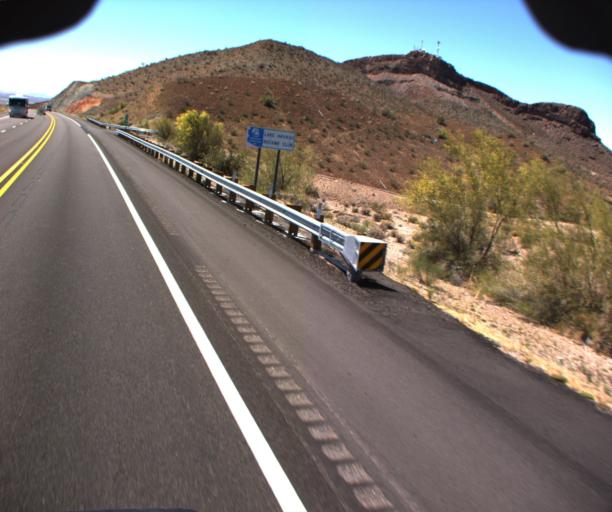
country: US
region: Arizona
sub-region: Mohave County
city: Desert Hills
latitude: 34.6045
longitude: -114.3632
